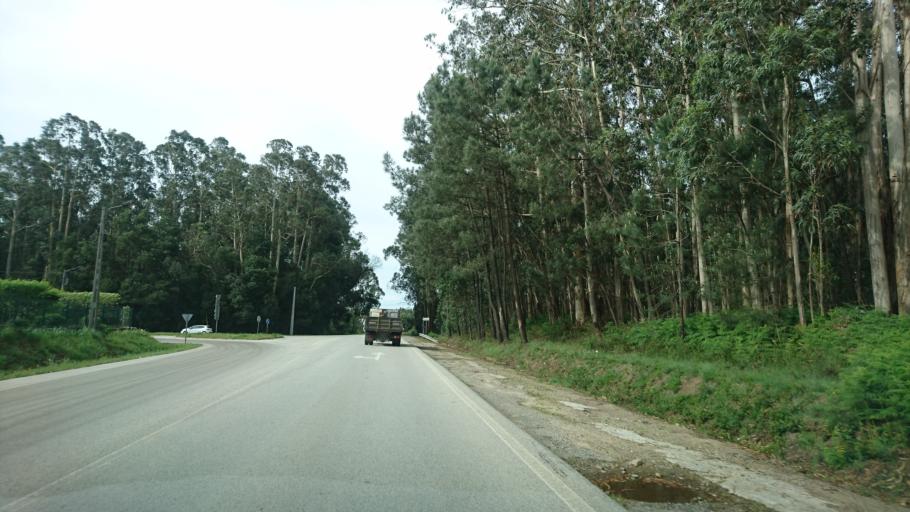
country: PT
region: Aveiro
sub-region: Albergaria-A-Velha
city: Albergaria-a-Velha
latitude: 40.6930
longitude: -8.5168
